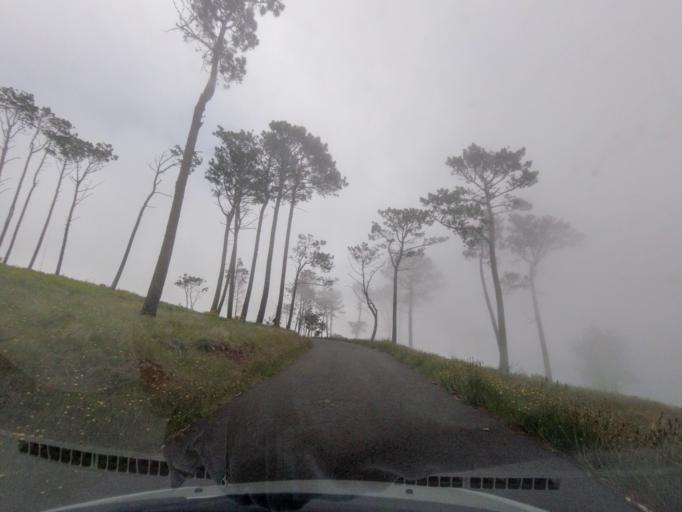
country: PT
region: Madeira
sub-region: Funchal
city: Nossa Senhora do Monte
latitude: 32.7078
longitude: -16.9108
